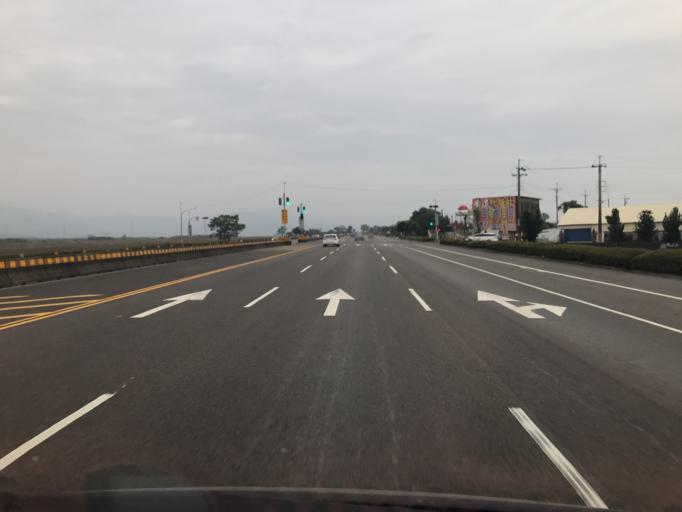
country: TW
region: Taiwan
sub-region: Pingtung
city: Pingtung
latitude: 22.4254
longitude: 120.5783
